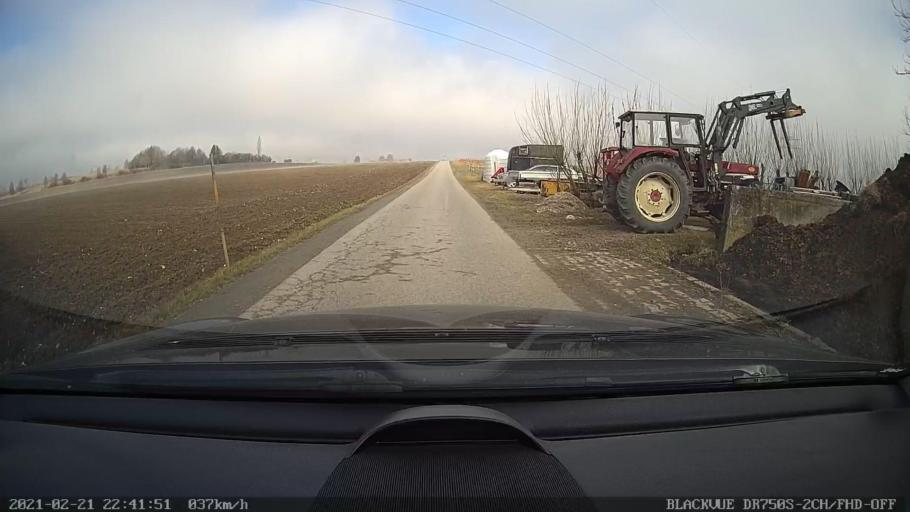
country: DE
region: Bavaria
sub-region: Upper Bavaria
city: Griesstatt
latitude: 47.9808
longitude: 12.1814
